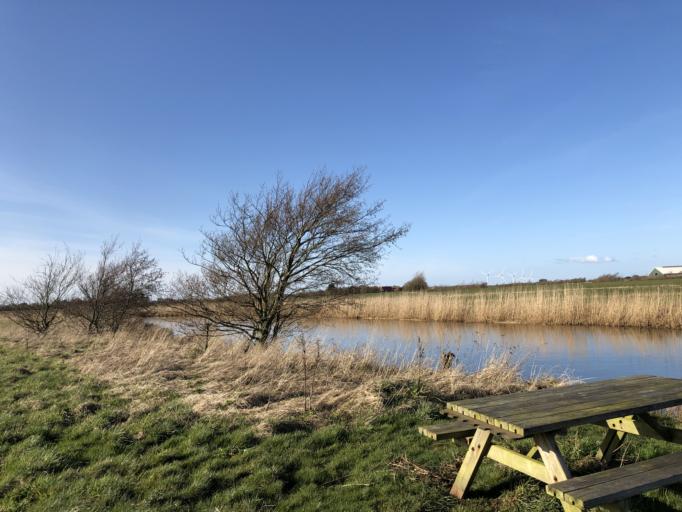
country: DK
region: Central Jutland
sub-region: Holstebro Kommune
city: Ulfborg
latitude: 56.3325
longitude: 8.3175
